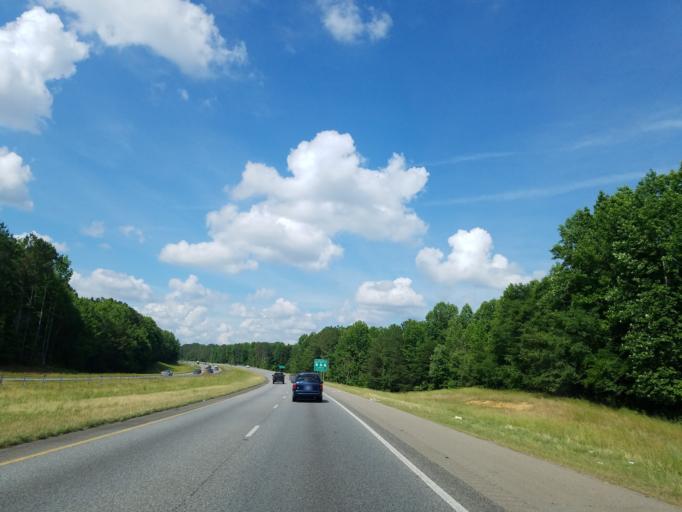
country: US
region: Georgia
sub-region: Cherokee County
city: Holly Springs
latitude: 34.1900
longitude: -84.5040
